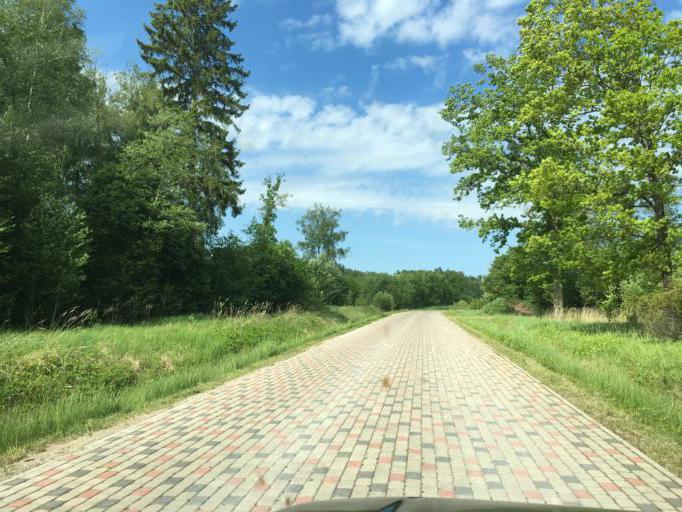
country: LV
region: Talsu Rajons
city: Valdemarpils
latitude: 57.3725
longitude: 22.5210
